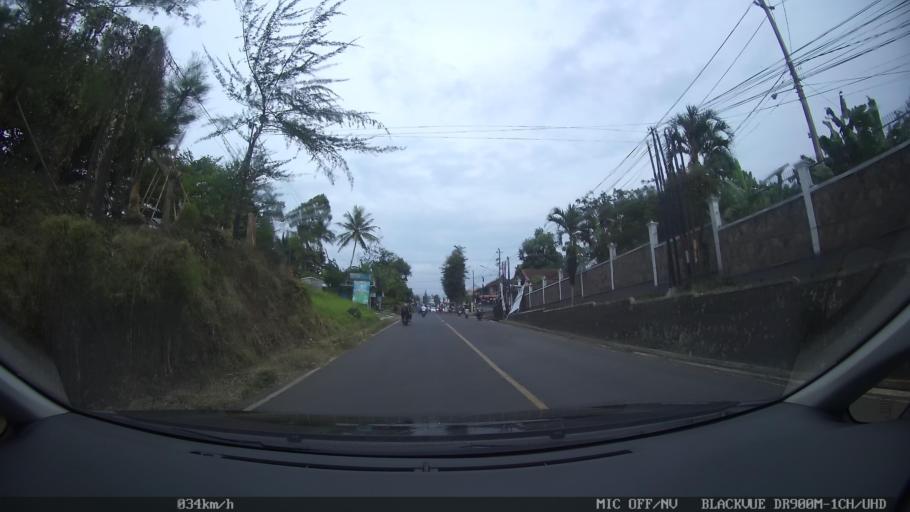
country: ID
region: Lampung
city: Kedaton
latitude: -5.3939
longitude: 105.2213
